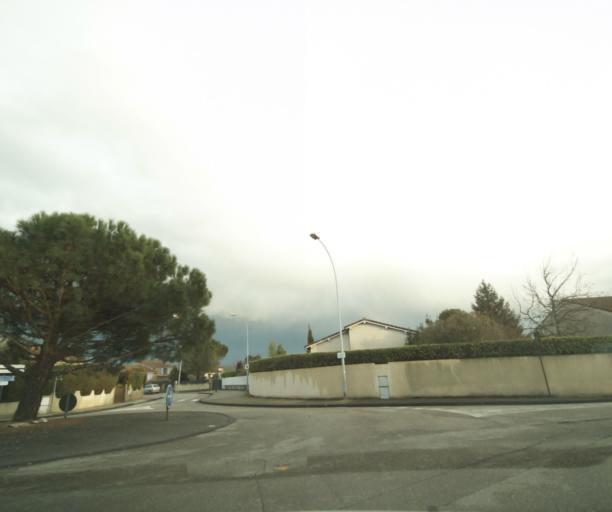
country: FR
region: Rhone-Alpes
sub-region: Departement de la Drome
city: Bourg-les-Valence
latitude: 44.9450
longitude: 4.9069
